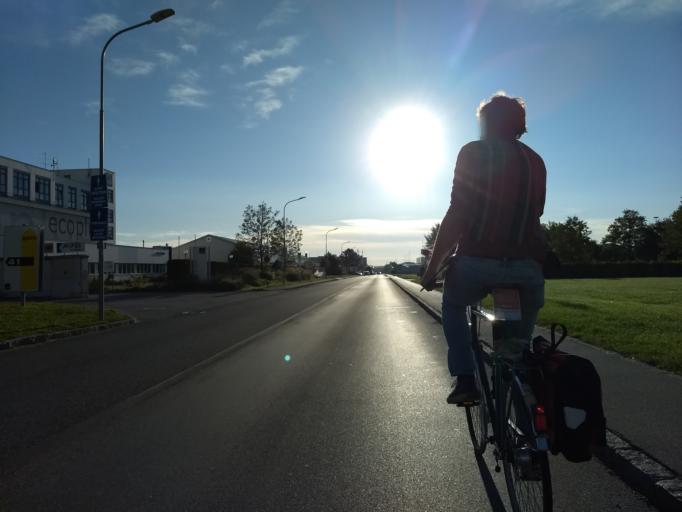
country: AT
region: Lower Austria
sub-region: Politischer Bezirk Modling
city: Wiener Neudorf
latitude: 48.0751
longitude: 16.3206
